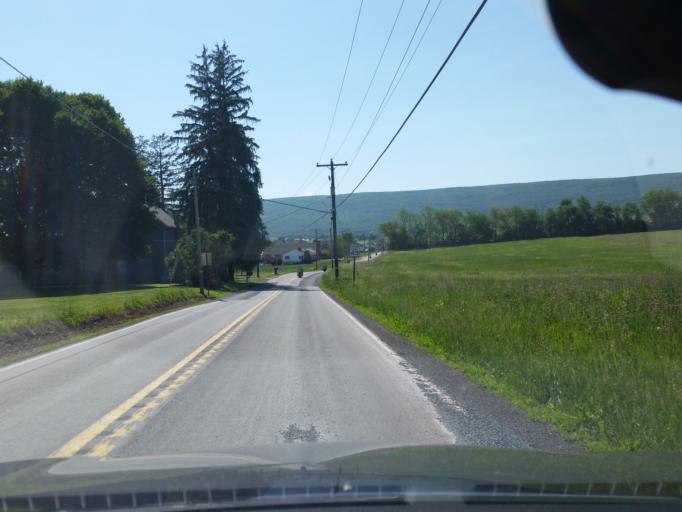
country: US
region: Pennsylvania
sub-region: Lycoming County
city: Duboistown
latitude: 41.1248
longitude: -77.0037
